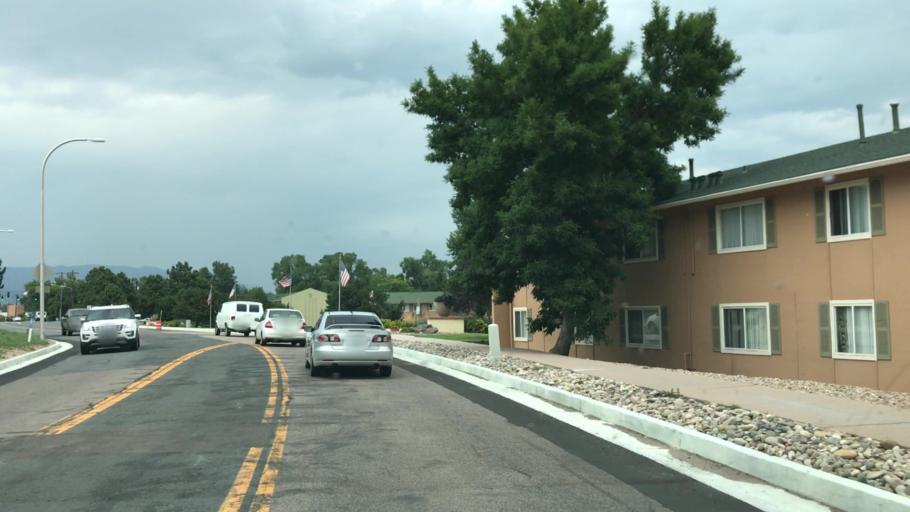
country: US
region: Colorado
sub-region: El Paso County
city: Colorado Springs
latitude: 38.8029
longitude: -104.8177
